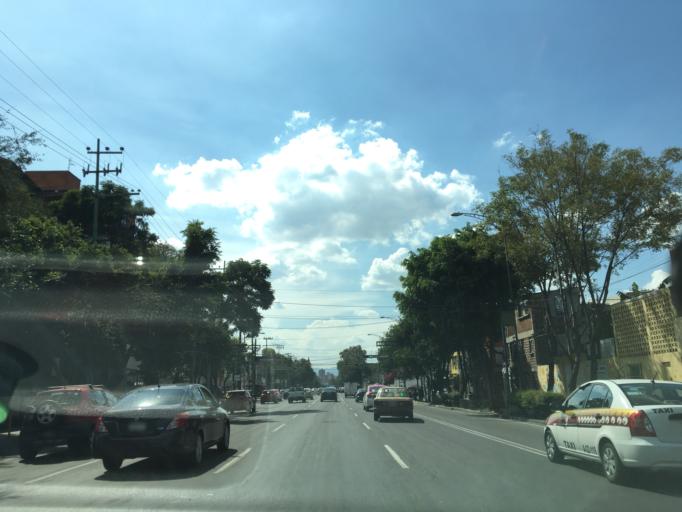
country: MX
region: Mexico City
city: Benito Juarez
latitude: 19.4070
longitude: -99.1487
